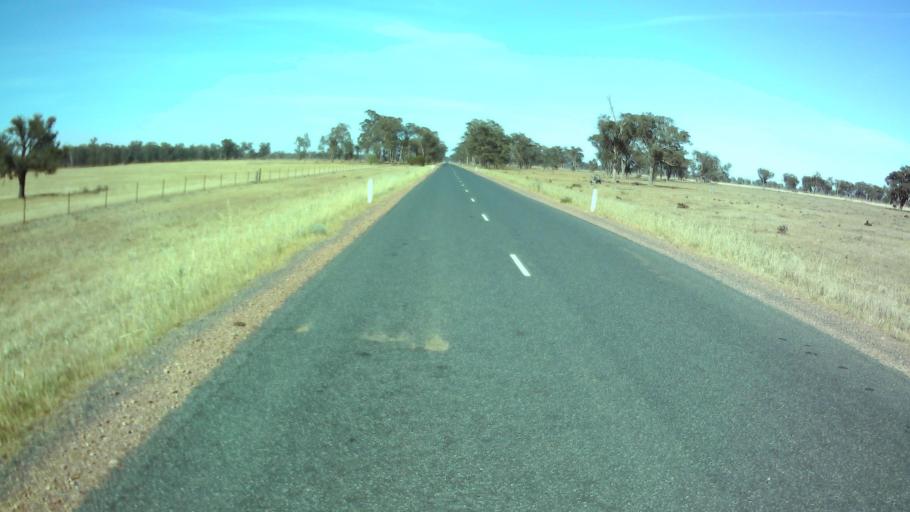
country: AU
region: New South Wales
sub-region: Weddin
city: Grenfell
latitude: -34.0998
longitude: 147.8783
